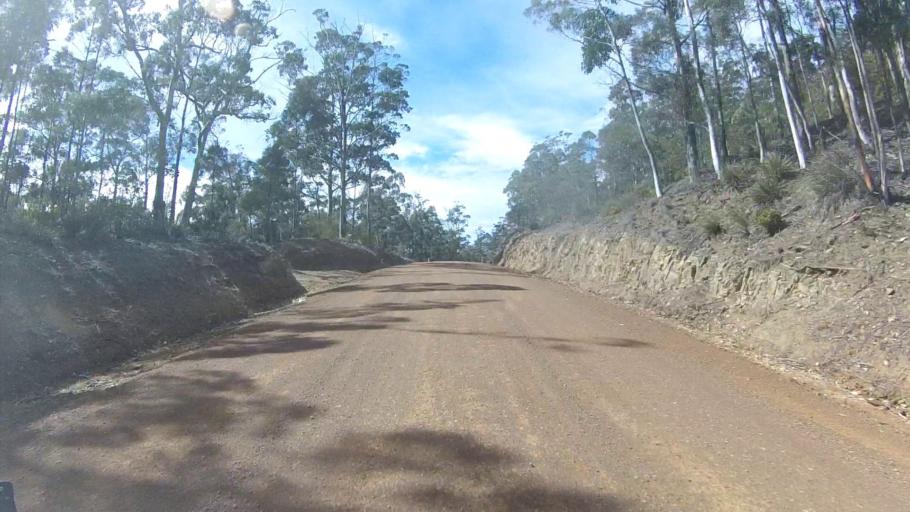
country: AU
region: Tasmania
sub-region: Sorell
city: Sorell
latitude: -42.6006
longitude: 147.8866
